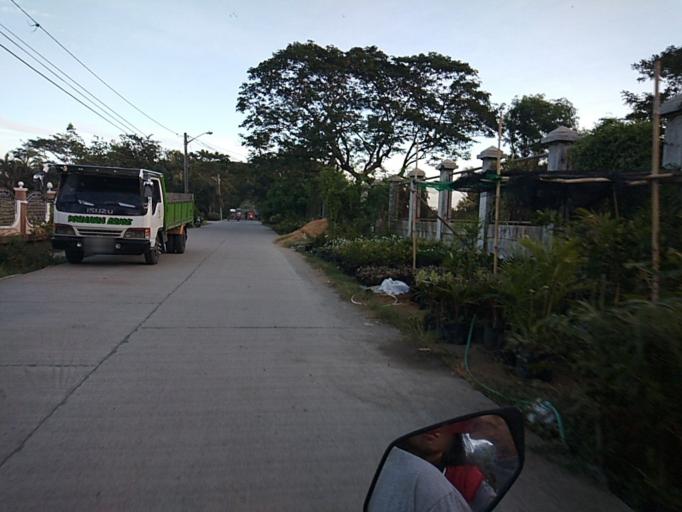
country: PH
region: Central Luzon
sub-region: Province of Bulacan
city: Paombong
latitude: 14.8620
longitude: 120.7658
